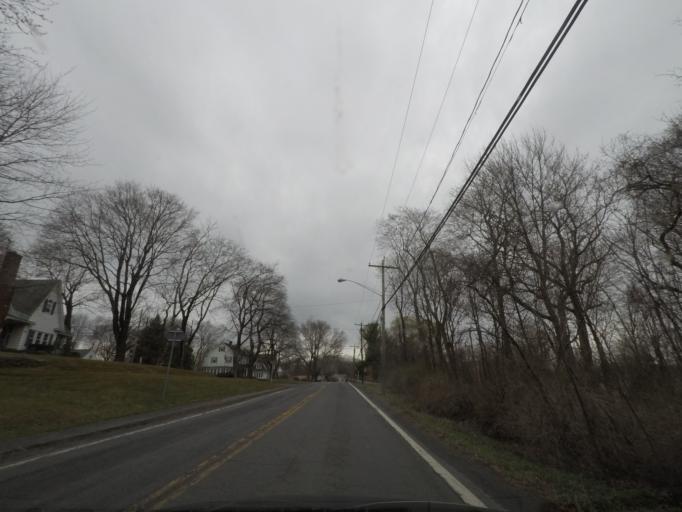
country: US
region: New York
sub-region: Albany County
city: Ravena
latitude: 42.5325
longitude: -73.8403
